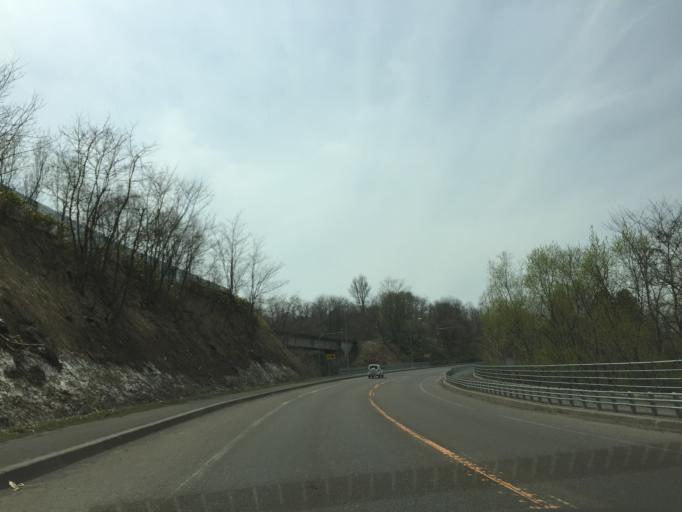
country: JP
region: Hokkaido
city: Akabira
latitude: 43.5361
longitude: 142.0990
